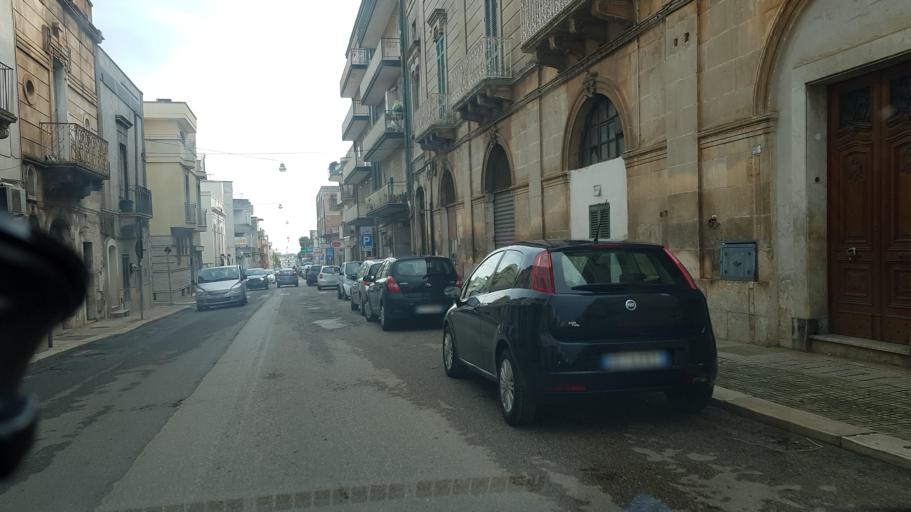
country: IT
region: Apulia
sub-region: Provincia di Brindisi
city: Carovigno
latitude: 40.7040
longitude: 17.6562
